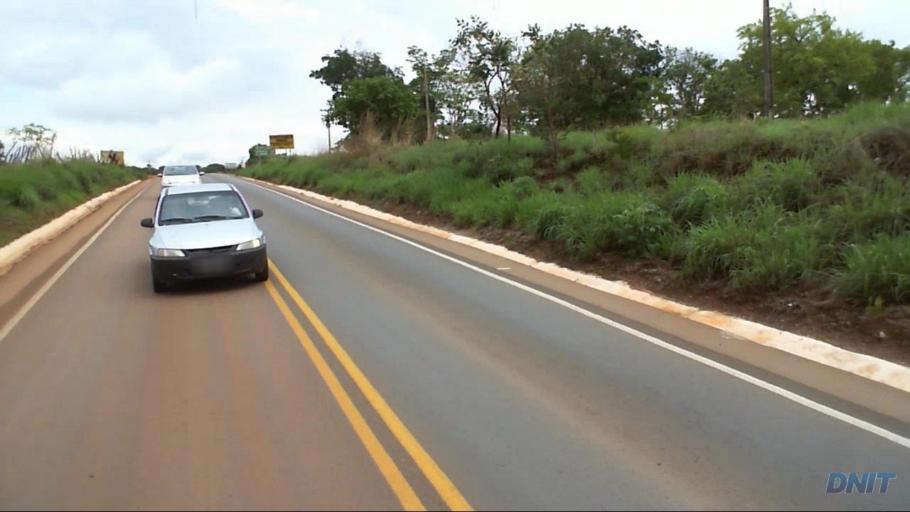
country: BR
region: Goias
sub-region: Padre Bernardo
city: Padre Bernardo
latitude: -15.3678
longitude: -48.2206
